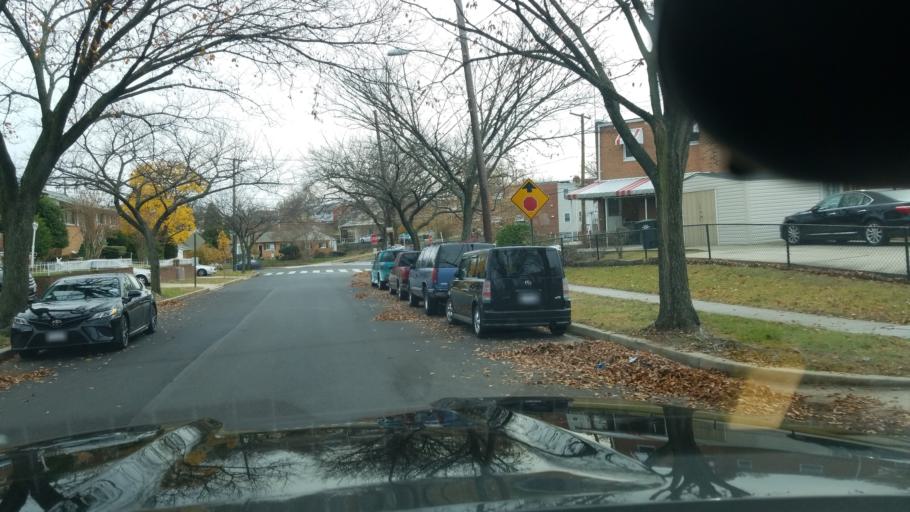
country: US
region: Maryland
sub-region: Prince George's County
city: Chillum
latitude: 38.9578
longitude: -76.9949
